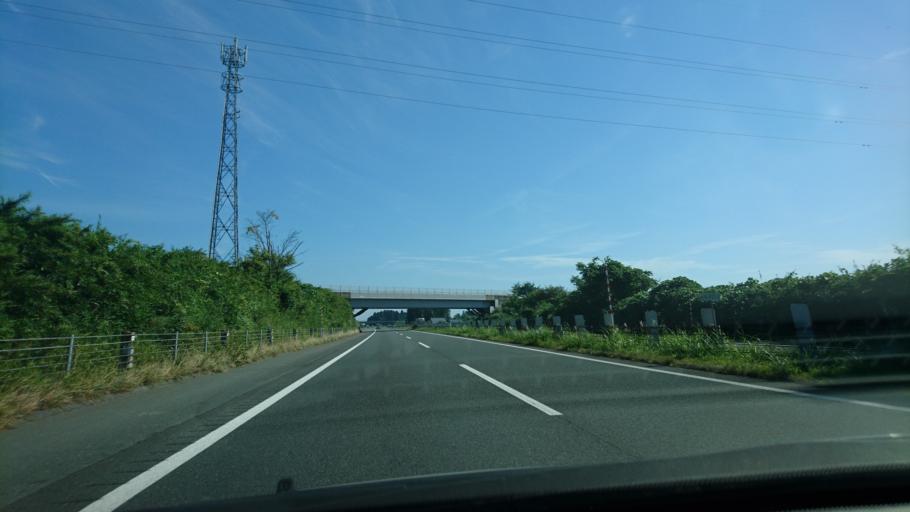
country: JP
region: Iwate
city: Mizusawa
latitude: 39.0950
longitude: 141.1129
